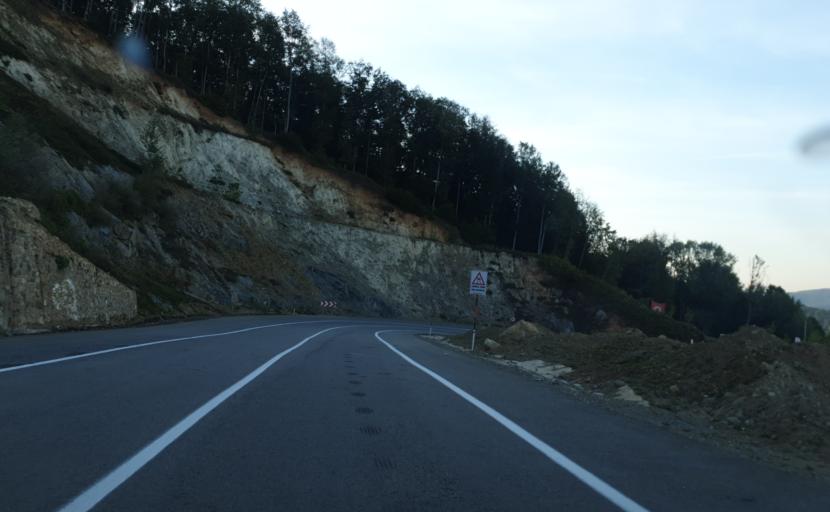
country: TR
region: Kirklareli
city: Sergen
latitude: 41.8142
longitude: 27.7449
